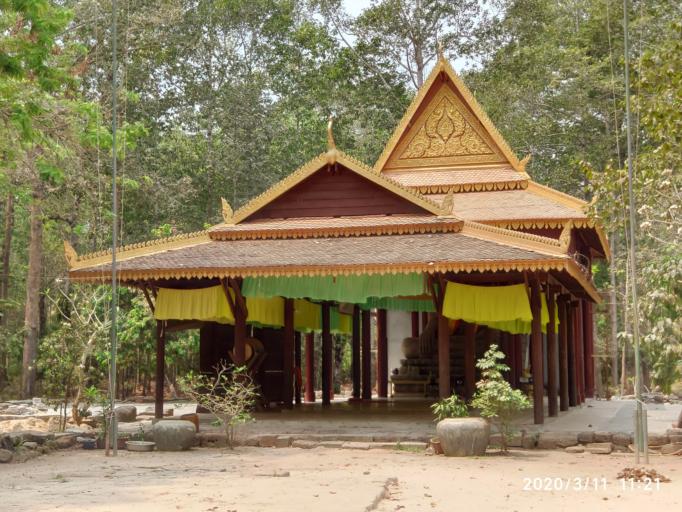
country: KH
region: Siem Reap
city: Siem Reap
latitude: 13.4485
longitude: 103.8580
